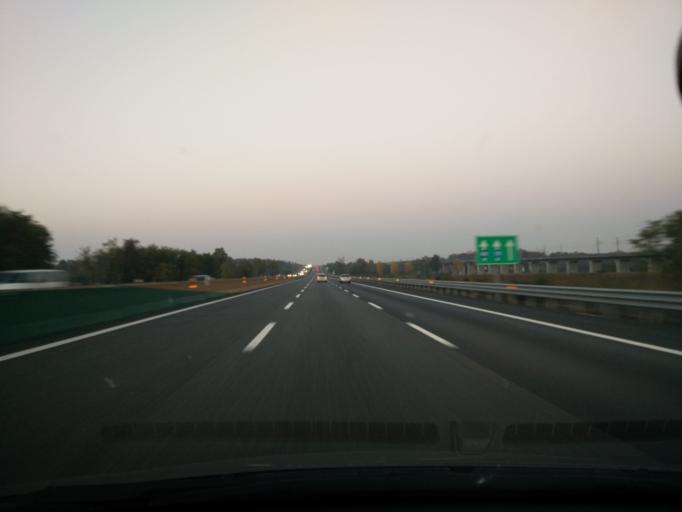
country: IT
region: Piedmont
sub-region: Provincia di Vercelli
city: Santhia
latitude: 45.3920
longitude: 8.1495
